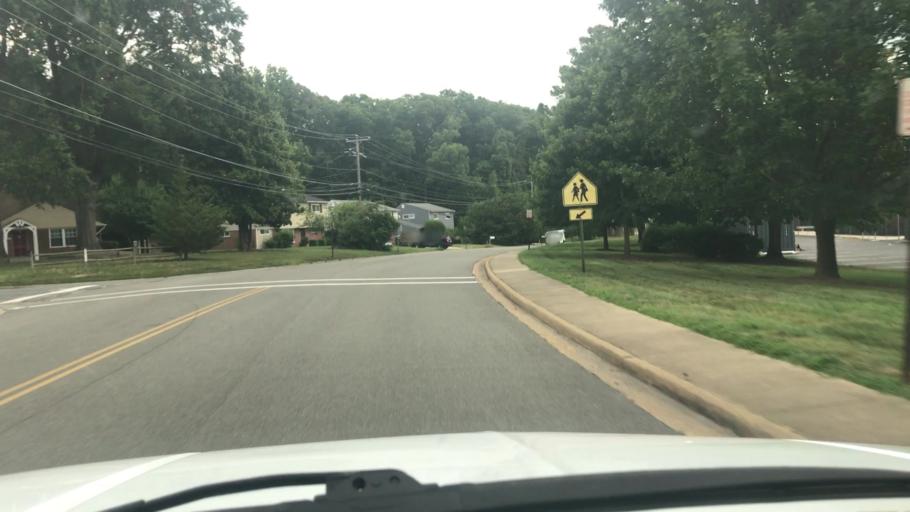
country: US
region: Virginia
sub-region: Henrico County
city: Tuckahoe
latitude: 37.6024
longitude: -77.5867
